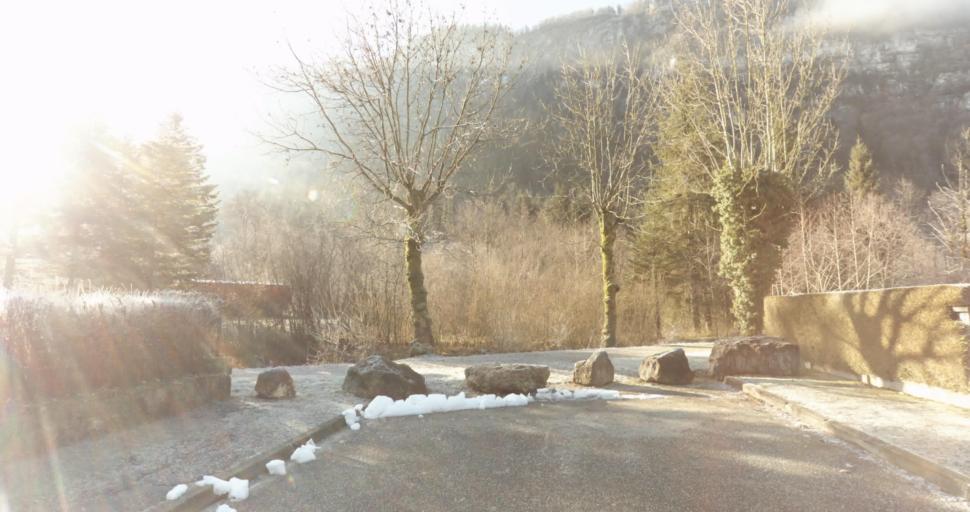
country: FR
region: Rhone-Alpes
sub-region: Departement de l'Ain
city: Nantua
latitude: 46.1499
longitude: 5.6033
